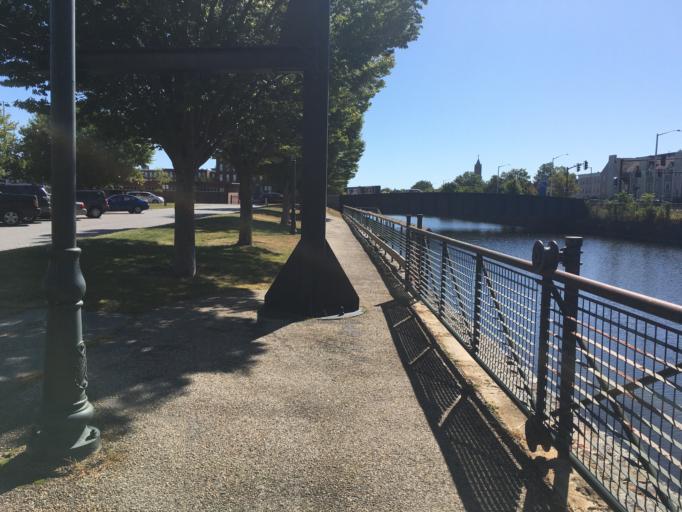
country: US
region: Massachusetts
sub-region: Middlesex County
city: Lowell
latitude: 42.6510
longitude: -71.3199
